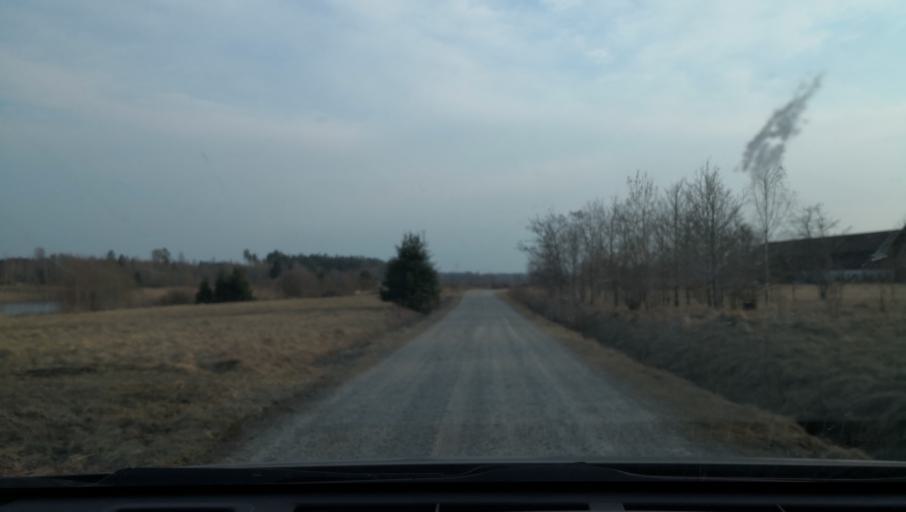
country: SE
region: OErebro
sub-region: Orebro Kommun
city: Hovsta
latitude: 59.3888
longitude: 15.2697
